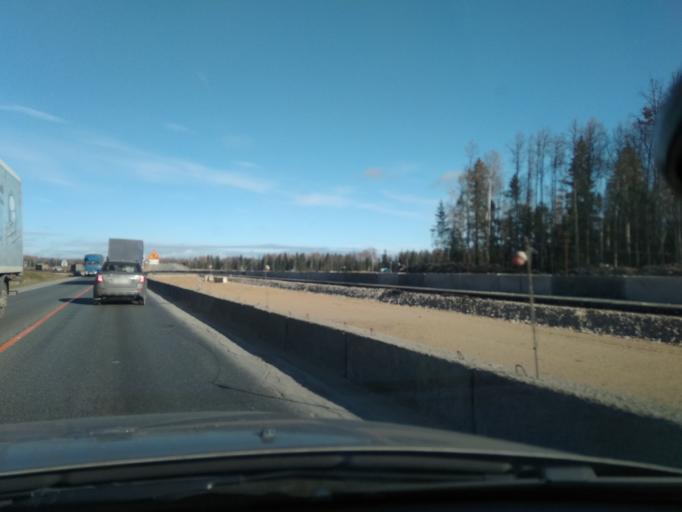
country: RU
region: Moskovskaya
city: Povarovo
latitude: 56.0009
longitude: 37.0247
